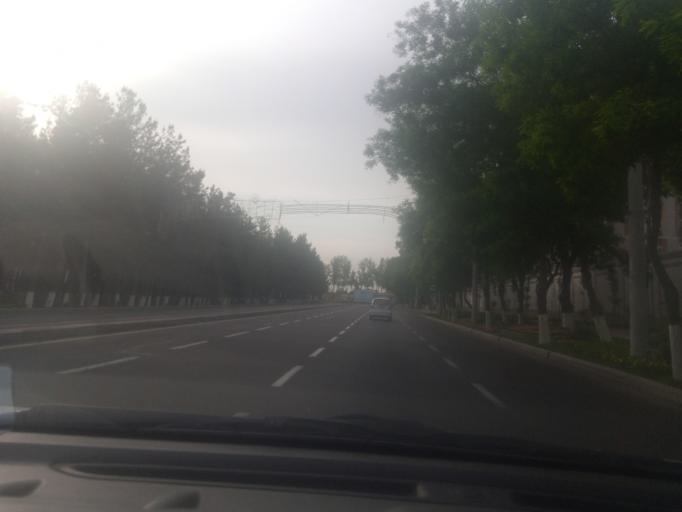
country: UZ
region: Toshkent
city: Salor
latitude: 41.3243
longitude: 69.3624
